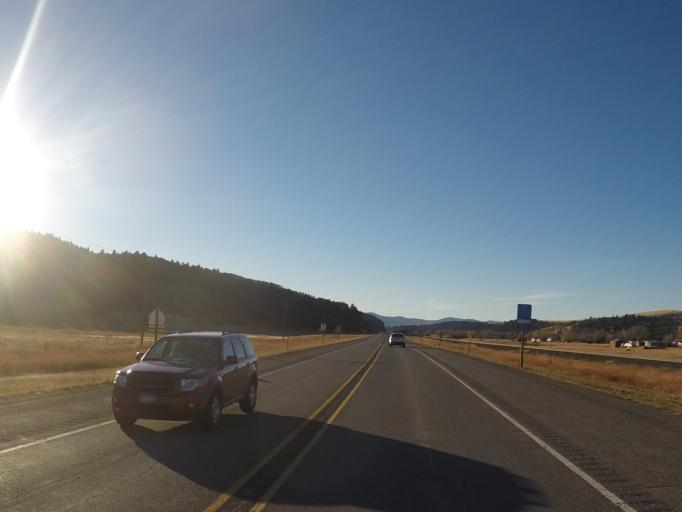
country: US
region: Montana
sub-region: Lewis and Clark County
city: Helena West Side
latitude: 46.5619
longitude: -112.4330
